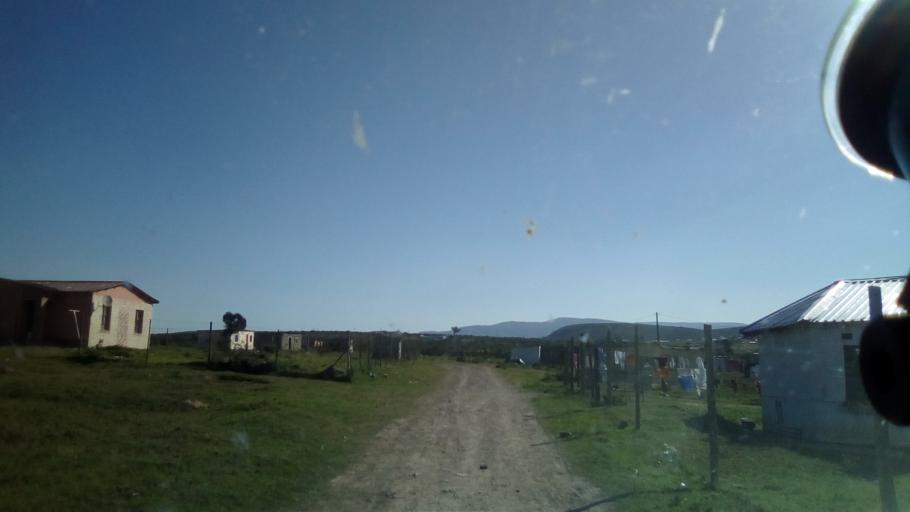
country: ZA
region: Eastern Cape
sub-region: Buffalo City Metropolitan Municipality
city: Bhisho
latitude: -32.8311
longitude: 27.3677
